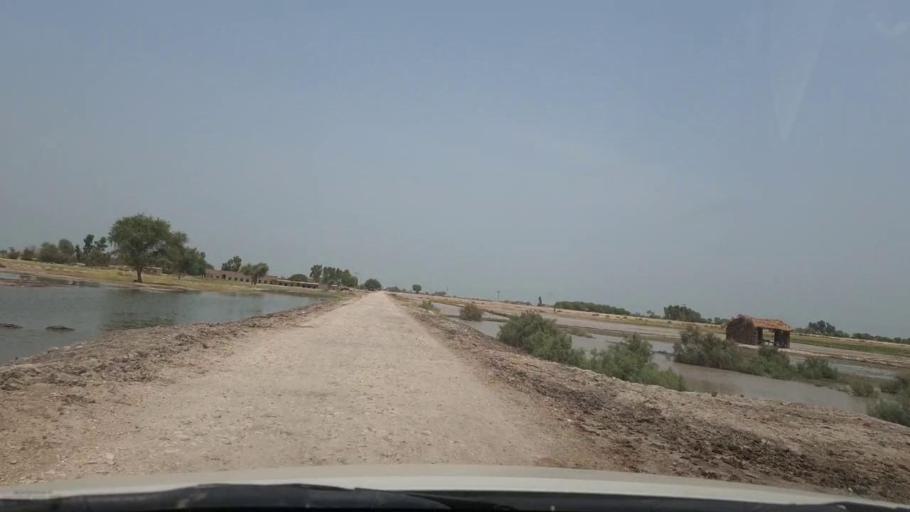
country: PK
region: Sindh
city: Rustam jo Goth
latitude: 28.0755
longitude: 68.8179
